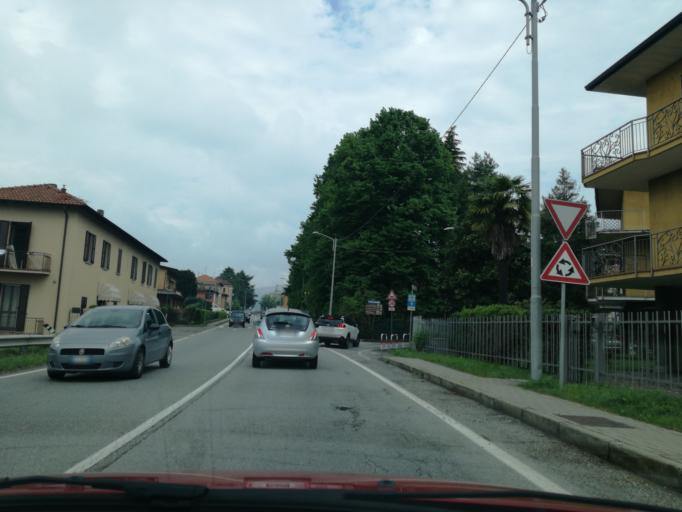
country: IT
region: Lombardy
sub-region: Provincia di Lecco
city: Cernusco Lombardone
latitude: 45.7047
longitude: 9.4113
